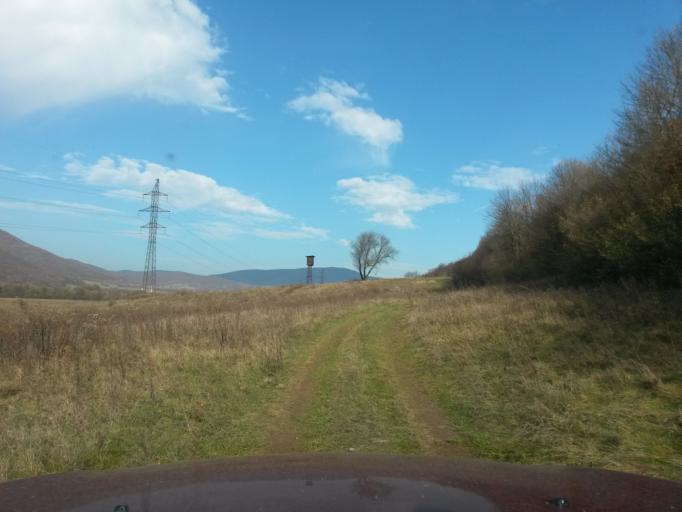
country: SK
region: Kosicky
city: Roznava
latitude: 48.5958
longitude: 20.4841
